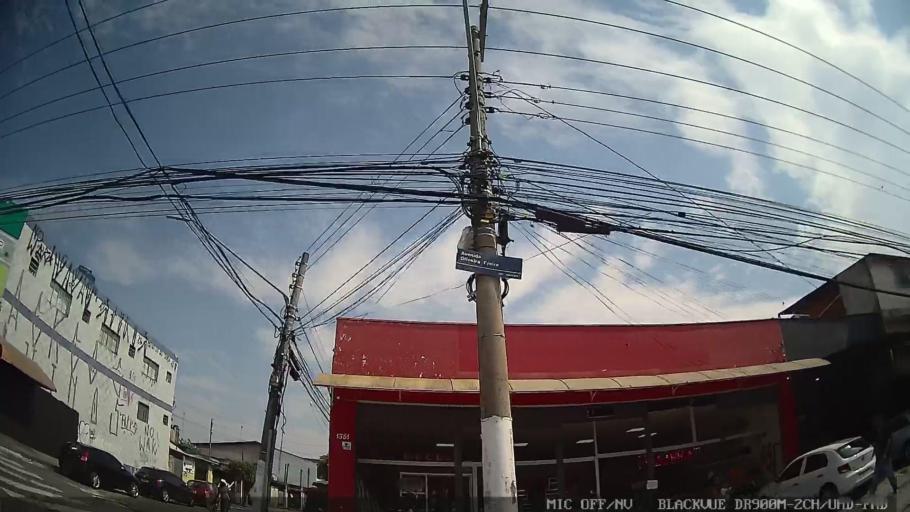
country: BR
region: Sao Paulo
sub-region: Itaquaquecetuba
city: Itaquaquecetuba
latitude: -23.4843
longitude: -46.4227
